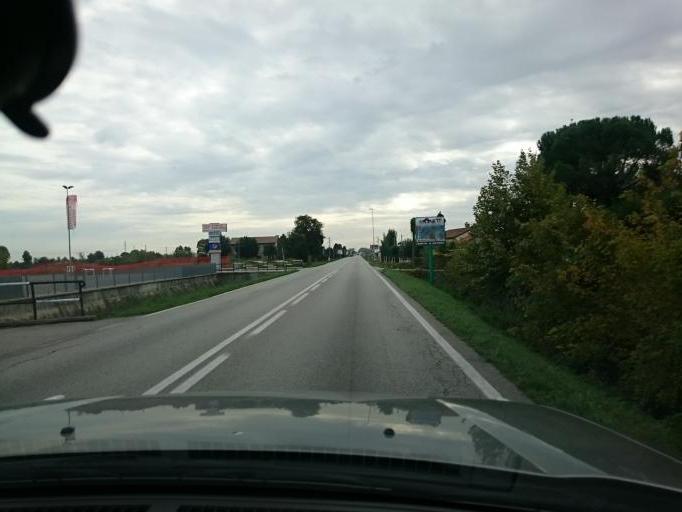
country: IT
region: Veneto
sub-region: Provincia di Padova
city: Sant'Angelo di Piove di Sacco
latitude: 45.3119
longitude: 12.0131
